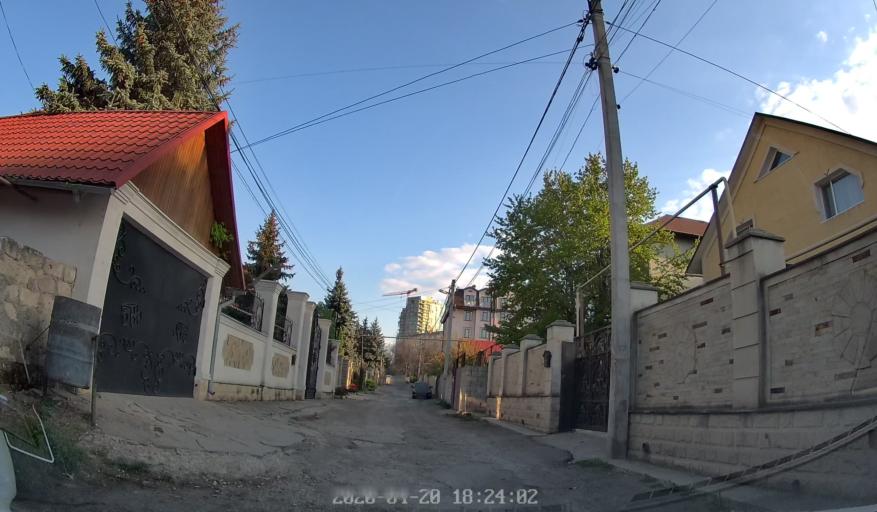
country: MD
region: Chisinau
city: Chisinau
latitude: 46.9948
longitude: 28.8377
